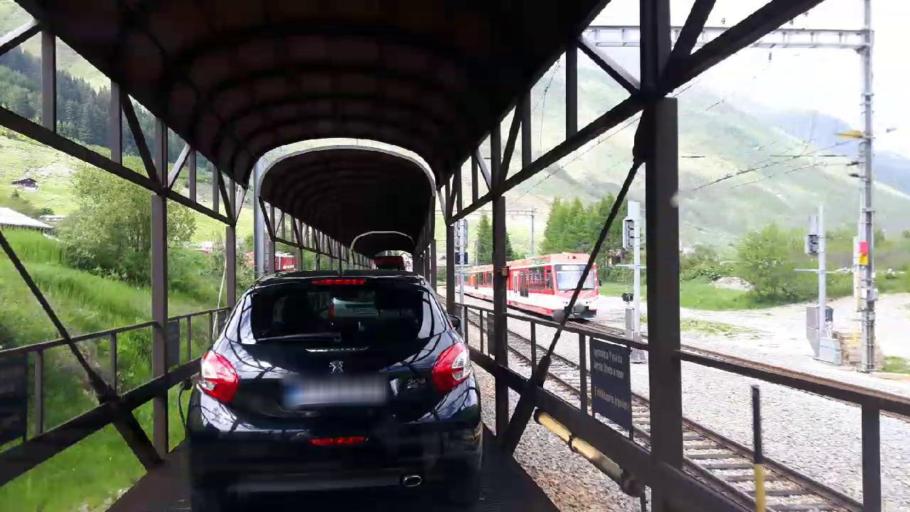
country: CH
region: Uri
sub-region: Uri
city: Andermatt
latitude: 46.5947
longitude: 8.5014
